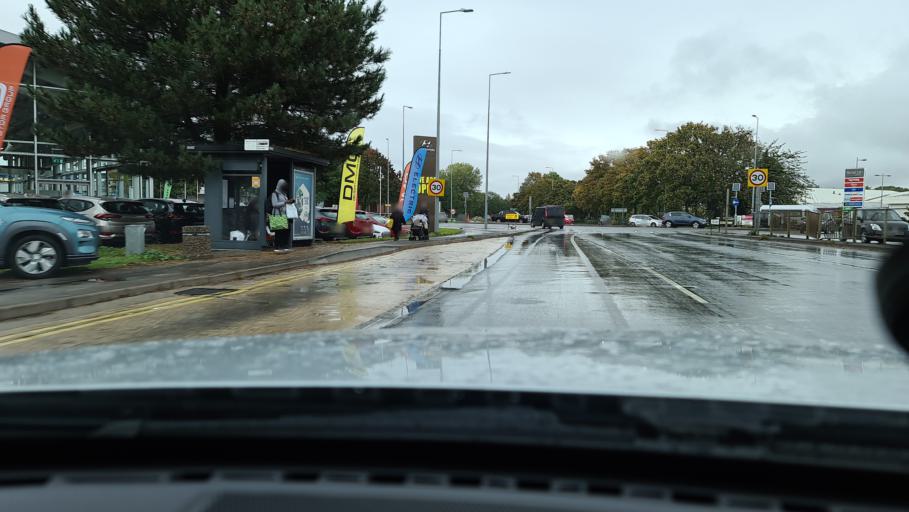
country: GB
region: England
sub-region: Buckinghamshire
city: Bletchley
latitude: 52.0020
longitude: -0.7266
